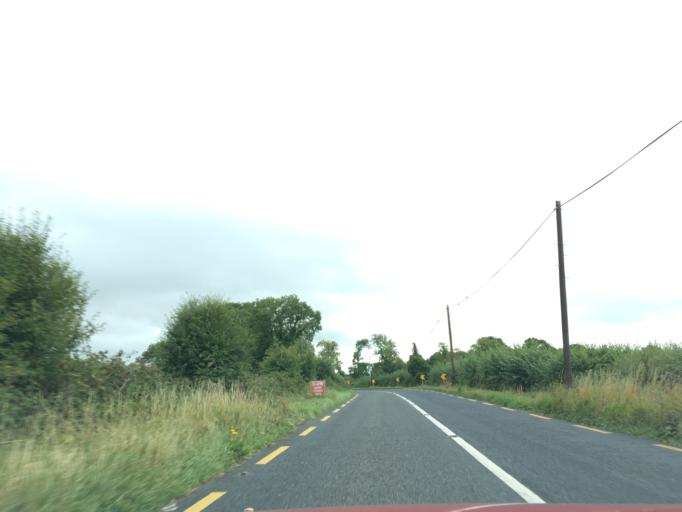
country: IE
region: Munster
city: Fethard
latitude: 52.4393
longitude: -7.7970
